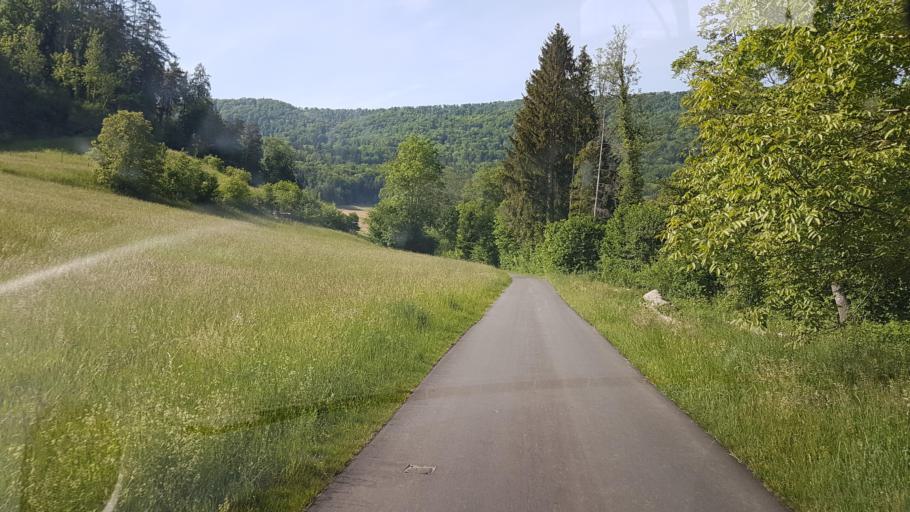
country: CH
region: Zurich
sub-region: Bezirk Dielsdorf
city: Otelfingen
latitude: 47.4672
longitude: 8.3870
